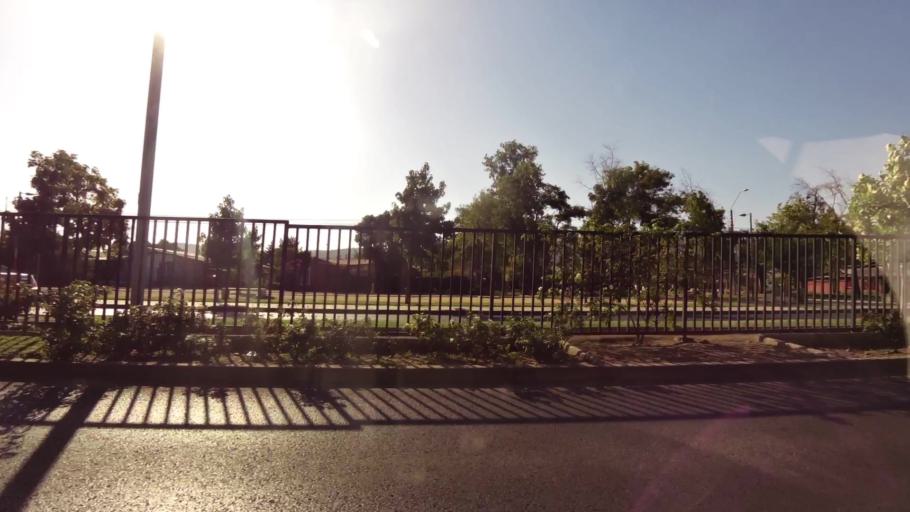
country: CL
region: Maule
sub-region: Provincia de Talca
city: Talca
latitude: -35.4330
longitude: -71.6784
